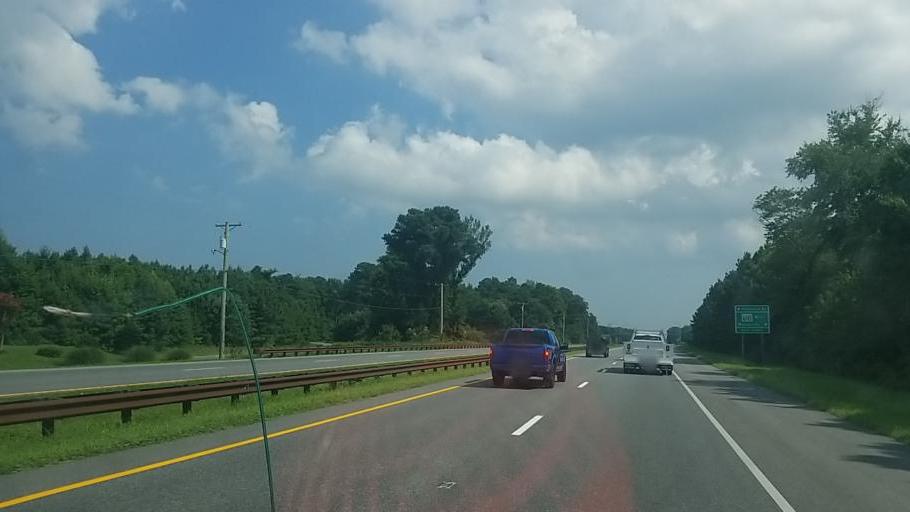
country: US
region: Delaware
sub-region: Sussex County
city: Selbyville
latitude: 38.4447
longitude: -75.2288
